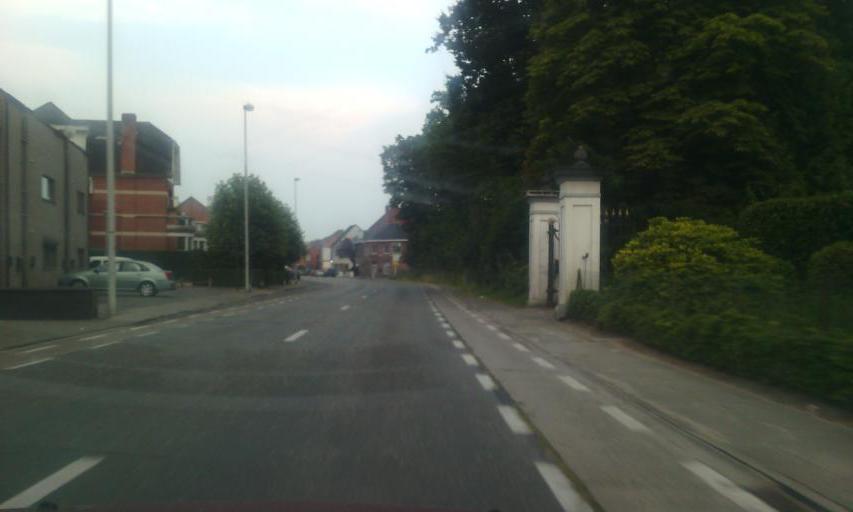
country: BE
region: Flanders
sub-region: Provincie Oost-Vlaanderen
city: Dendermonde
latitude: 51.0515
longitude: 4.1070
